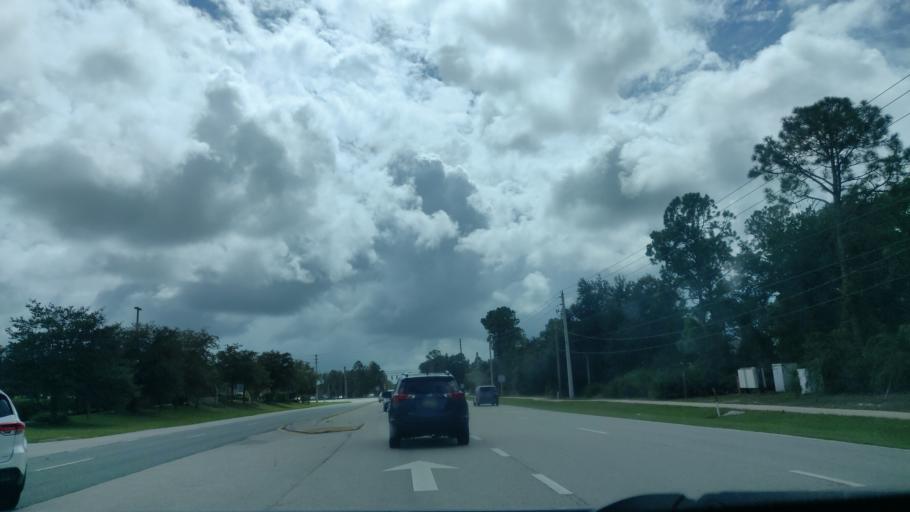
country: US
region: Florida
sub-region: Flagler County
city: Bunnell
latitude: 29.4777
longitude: -81.2213
